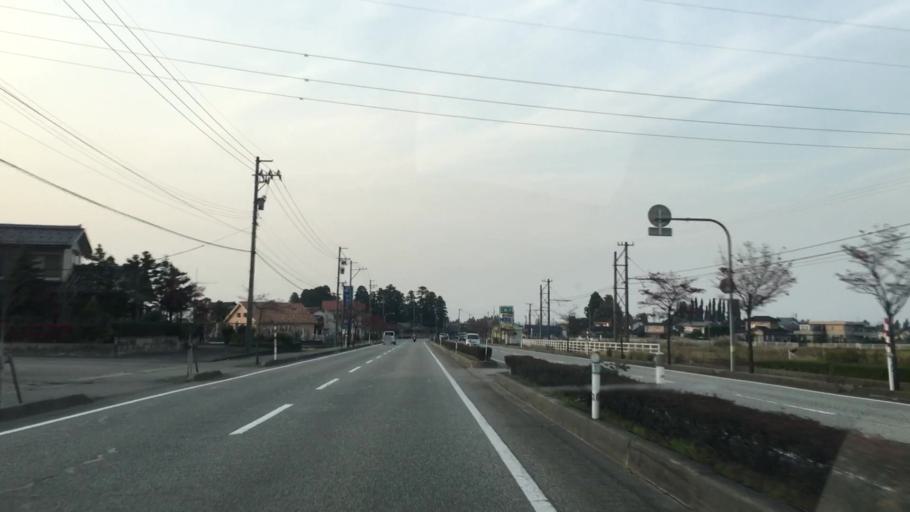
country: JP
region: Toyama
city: Toyama-shi
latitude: 36.6397
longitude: 137.2385
